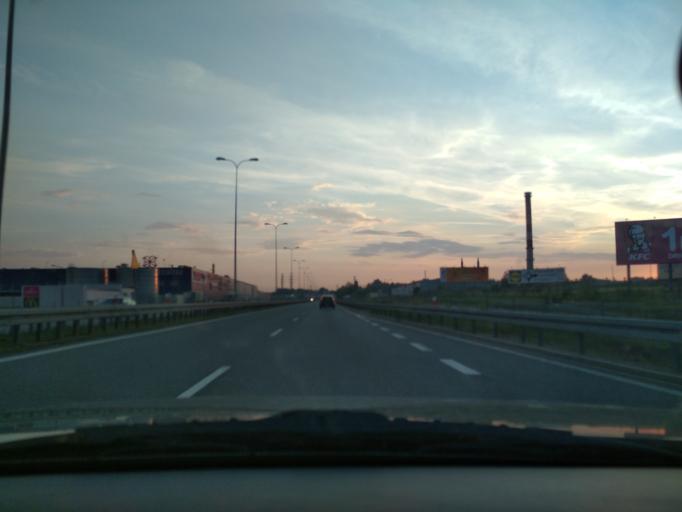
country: PL
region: Silesian Voivodeship
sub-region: Powiat gliwicki
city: Przyszowice
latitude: 50.2692
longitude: 18.7239
